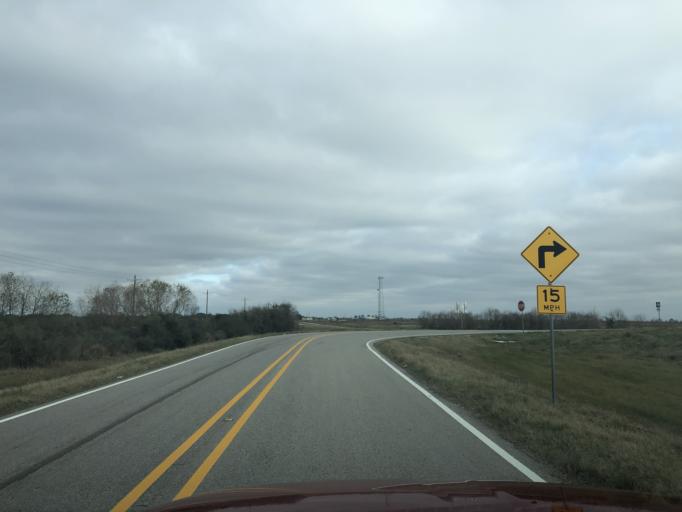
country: US
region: Texas
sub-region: Chambers County
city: Winnie
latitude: 29.8317
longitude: -94.4828
